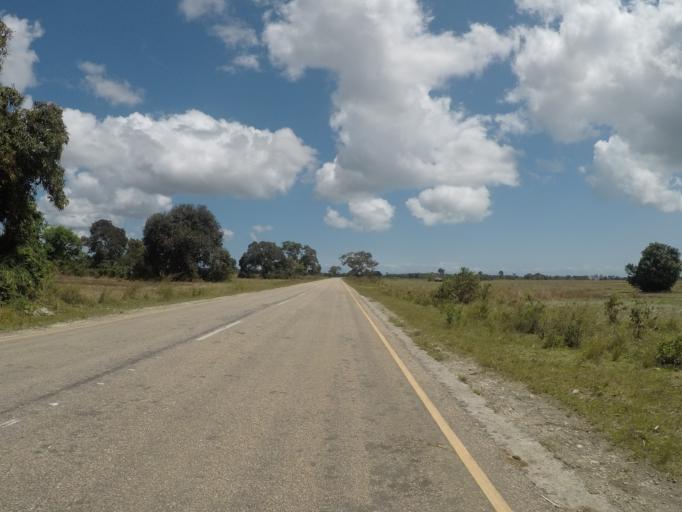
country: TZ
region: Zanzibar Central/South
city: Koani
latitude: -6.2116
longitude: 39.3657
